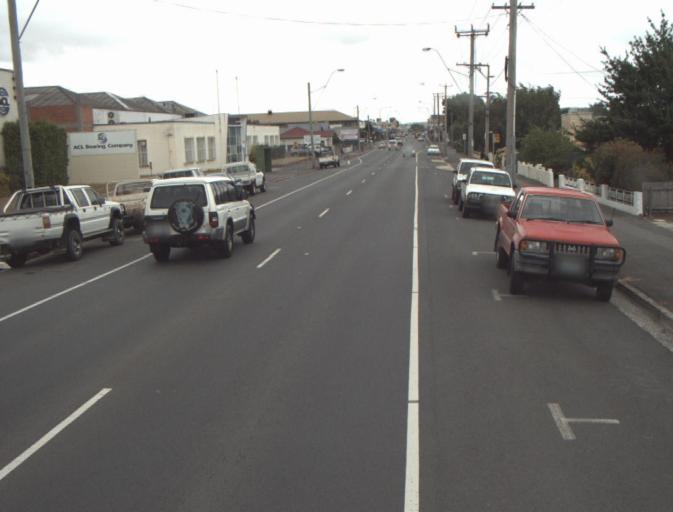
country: AU
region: Tasmania
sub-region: Launceston
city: Newnham
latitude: -41.4018
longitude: 147.1305
